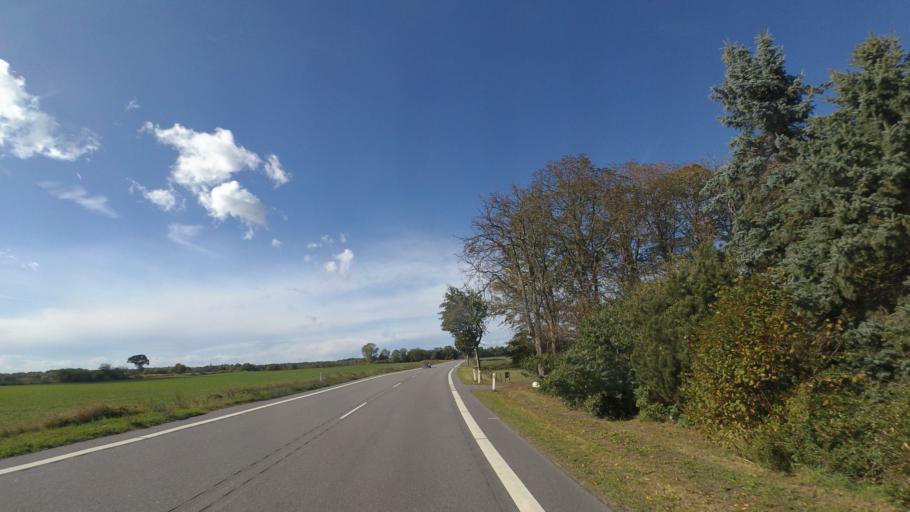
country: DK
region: Capital Region
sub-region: Bornholm Kommune
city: Ronne
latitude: 55.0751
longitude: 14.7791
